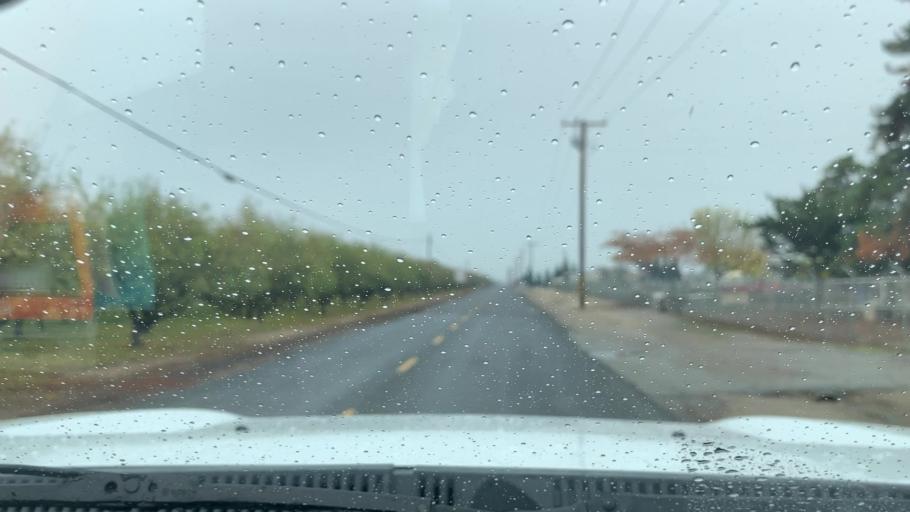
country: US
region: California
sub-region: Tulare County
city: Earlimart
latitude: 35.8339
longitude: -119.2582
